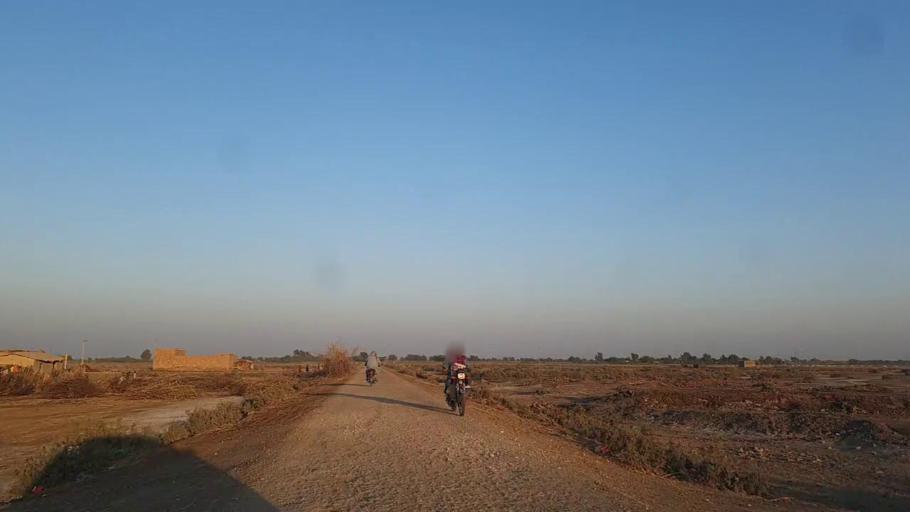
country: PK
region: Sindh
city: Samaro
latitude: 25.2977
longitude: 69.3889
